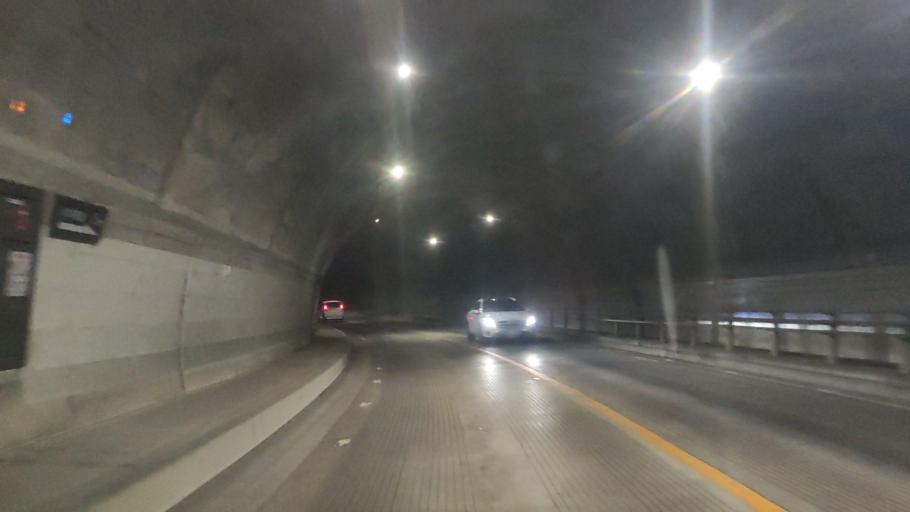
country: JP
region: Kumamoto
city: Hitoyoshi
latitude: 32.0741
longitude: 130.8015
